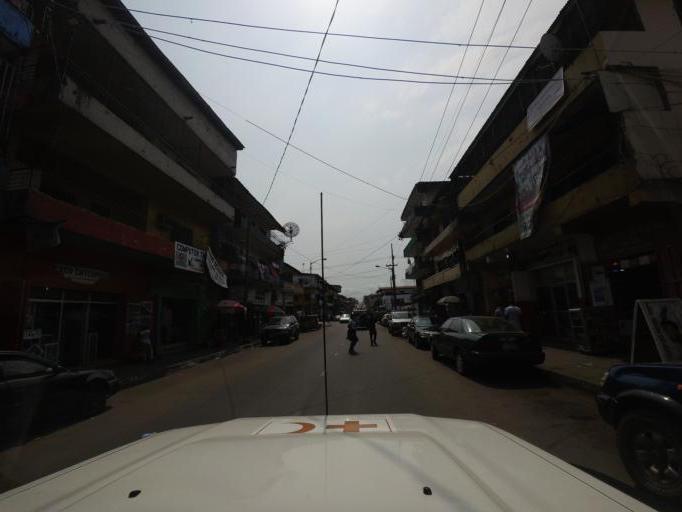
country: LR
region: Montserrado
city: Monrovia
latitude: 6.3150
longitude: -10.8057
